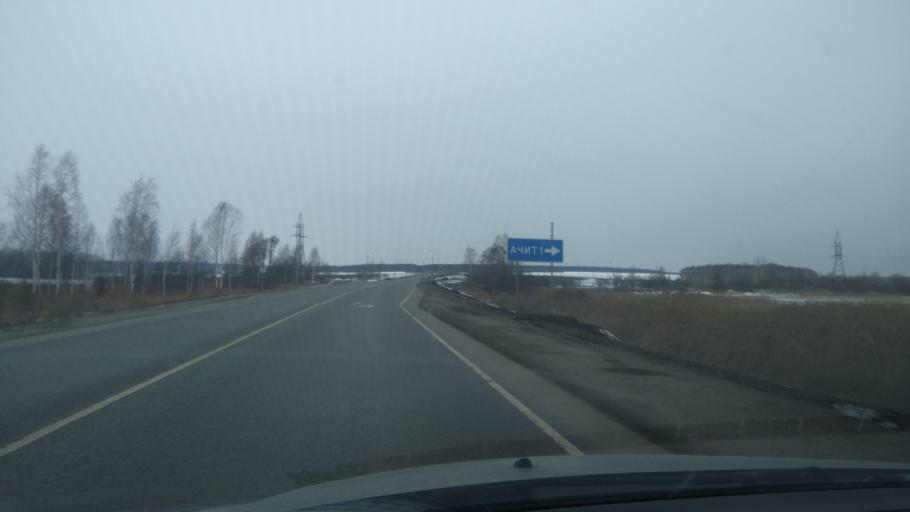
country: RU
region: Sverdlovsk
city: Achit
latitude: 56.7855
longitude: 57.8907
